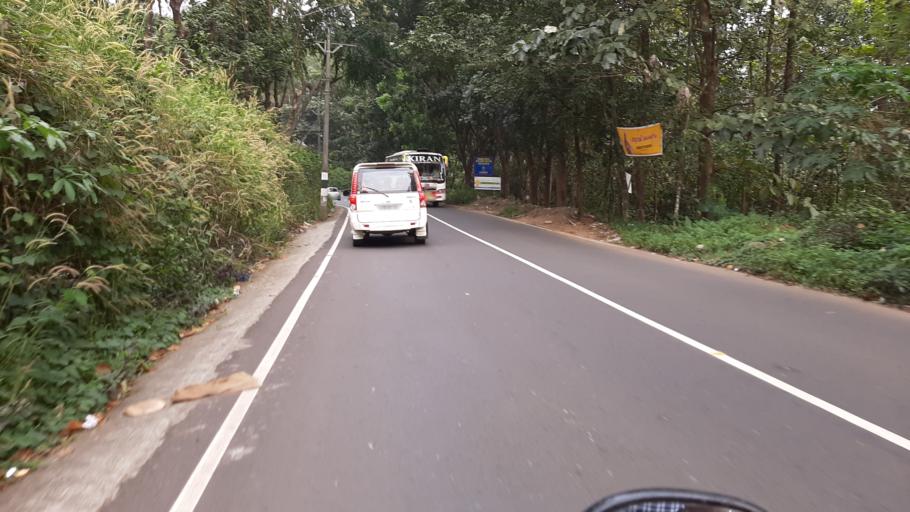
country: IN
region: Kerala
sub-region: Pattanamtitta
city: Pathanamthitta
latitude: 9.4507
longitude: 76.8705
